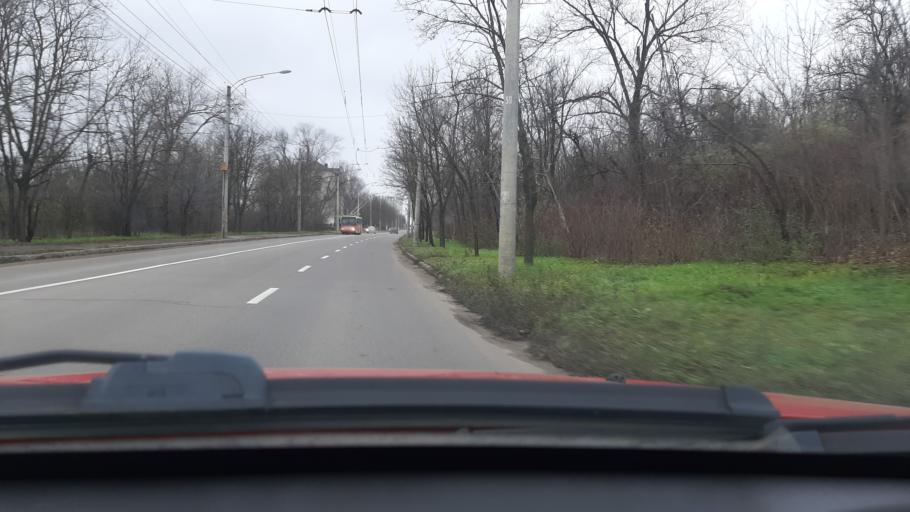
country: MD
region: Chisinau
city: Chisinau
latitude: 47.0561
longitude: 28.8149
